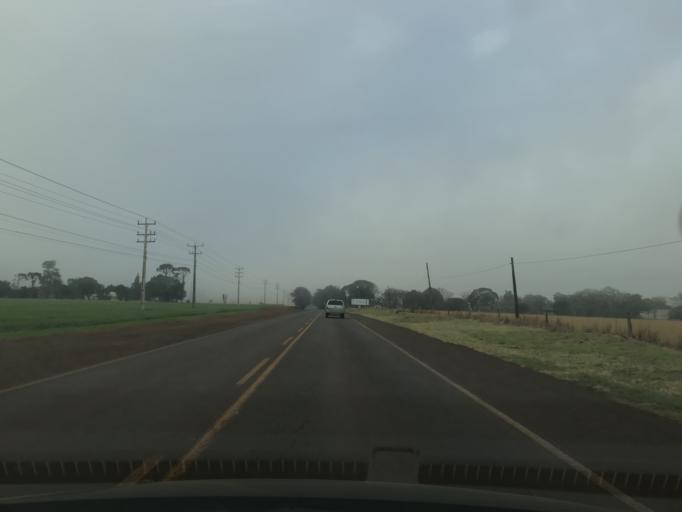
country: BR
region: Parana
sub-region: Toledo
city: Toledo
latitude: -24.6970
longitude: -53.6970
